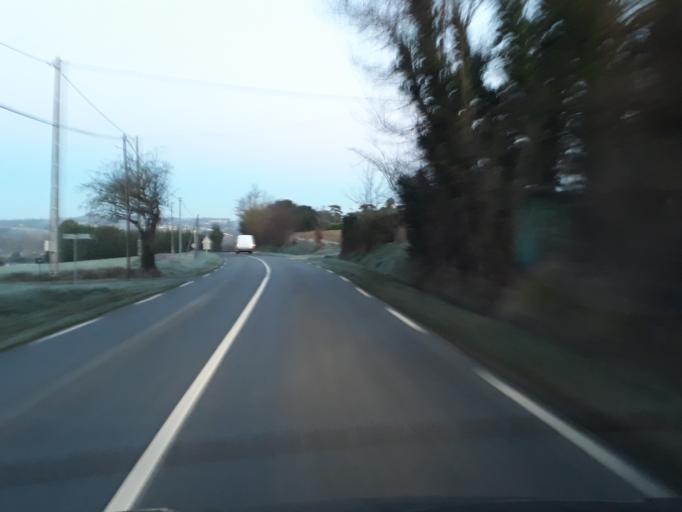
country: FR
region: Midi-Pyrenees
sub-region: Departement du Gers
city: Samatan
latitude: 43.4792
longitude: 0.9396
